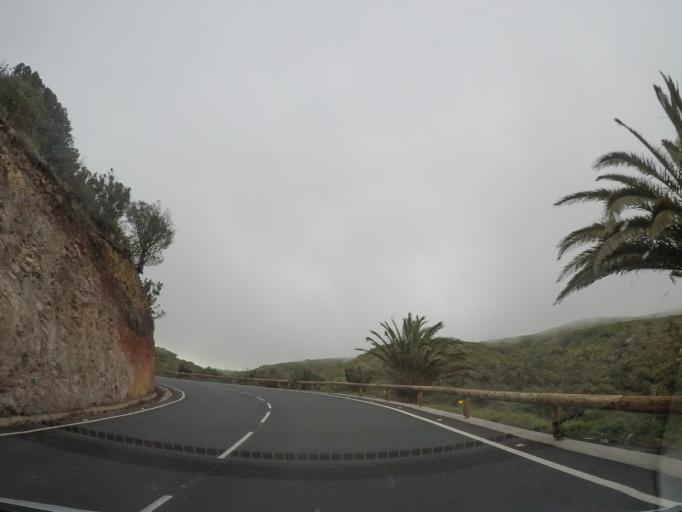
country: ES
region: Canary Islands
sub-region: Provincia de Santa Cruz de Tenerife
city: Vallehermosa
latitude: 28.1430
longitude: -17.3078
